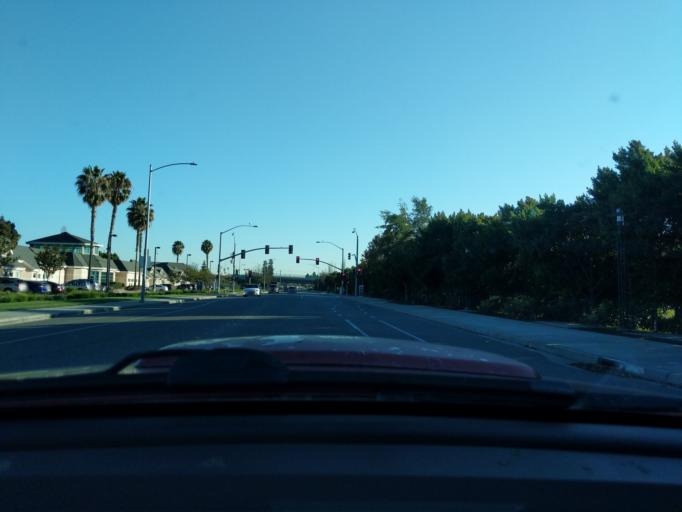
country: US
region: California
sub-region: Santa Clara County
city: Milpitas
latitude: 37.4183
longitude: -121.9160
